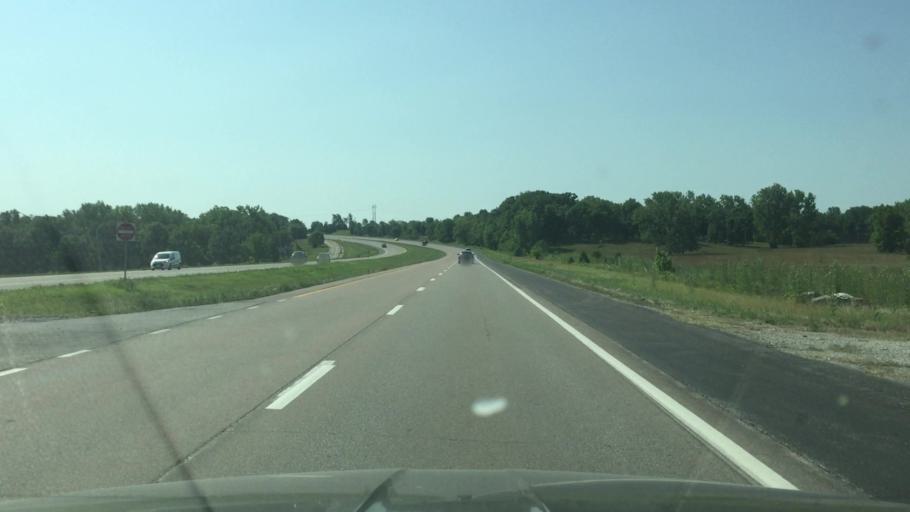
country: US
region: Missouri
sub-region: Pettis County
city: Sedalia
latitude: 38.7249
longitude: -93.3027
